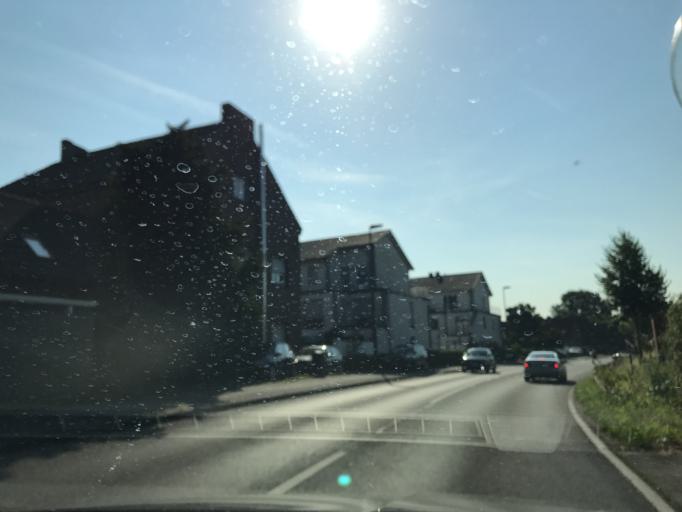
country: DE
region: North Rhine-Westphalia
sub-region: Regierungsbezirk Dusseldorf
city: Meerbusch
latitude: 51.2539
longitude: 6.7161
